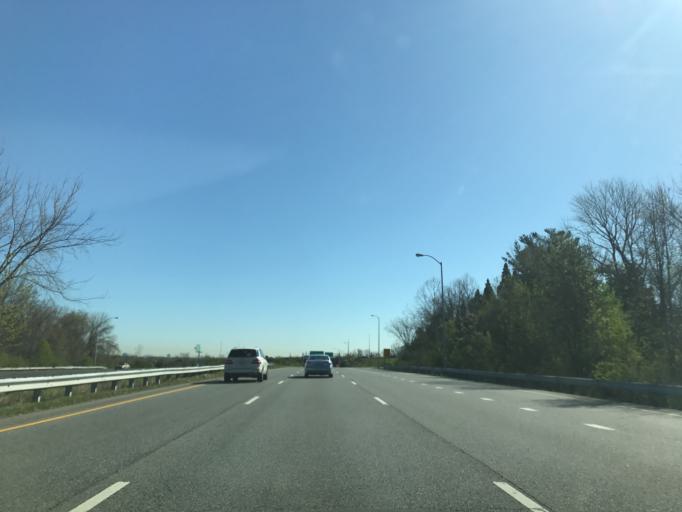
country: US
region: Maryland
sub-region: Anne Arundel County
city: Linthicum
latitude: 39.2179
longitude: -76.6623
